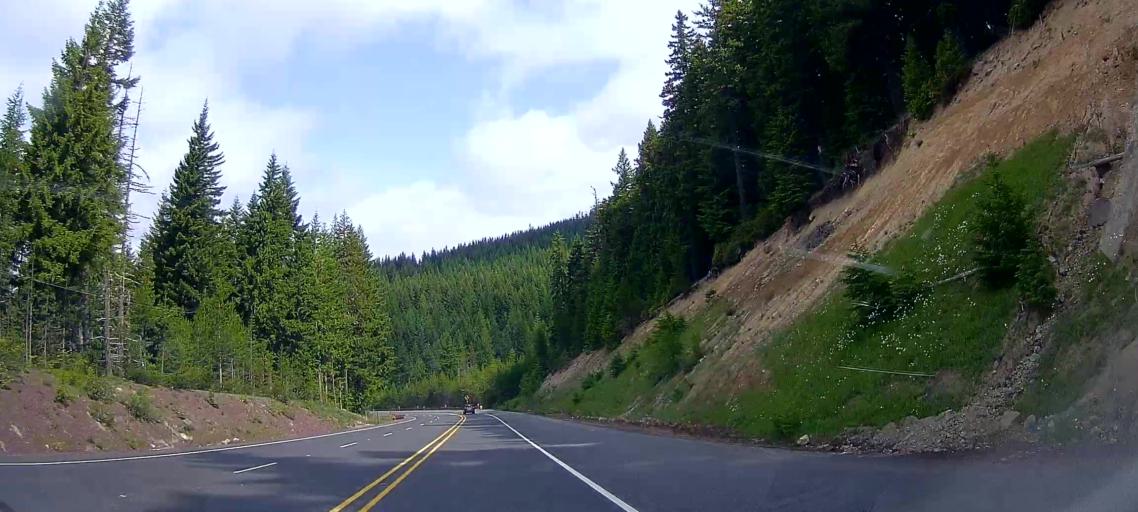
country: US
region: Oregon
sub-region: Clackamas County
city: Mount Hood Village
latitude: 45.2393
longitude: -121.6989
